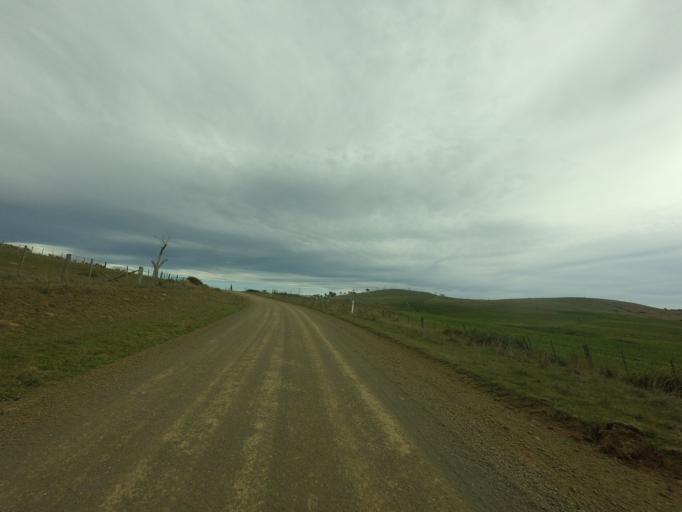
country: AU
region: Tasmania
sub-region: Derwent Valley
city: New Norfolk
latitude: -42.3875
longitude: 146.9802
